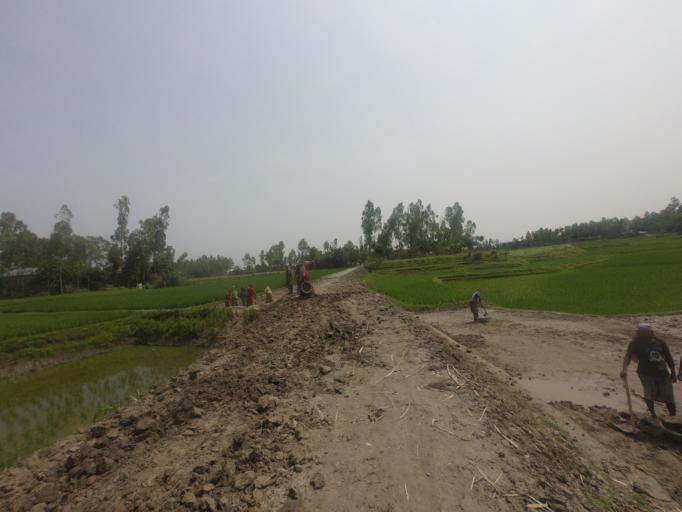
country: BD
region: Rajshahi
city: Sirajganj
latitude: 24.3579
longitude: 89.7208
